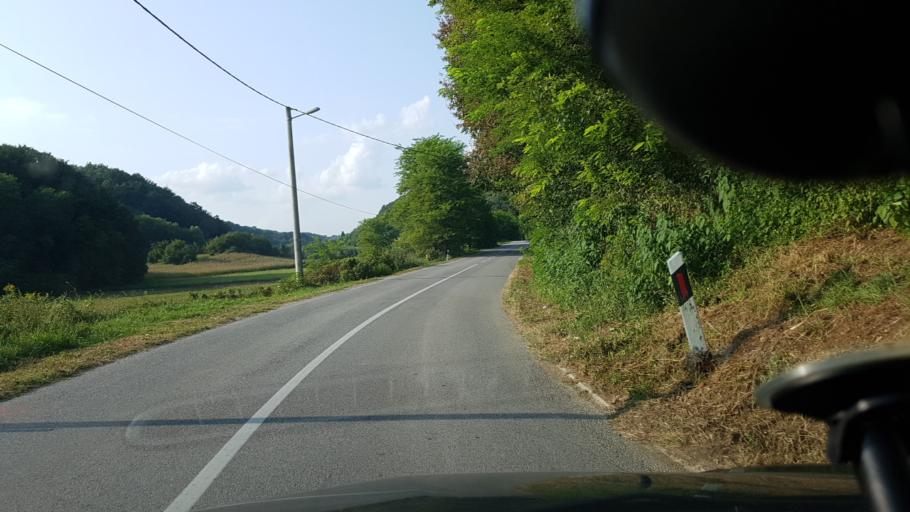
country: SI
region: Bistrica ob Sotli
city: Bistrica ob Sotli
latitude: 46.0389
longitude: 15.7738
